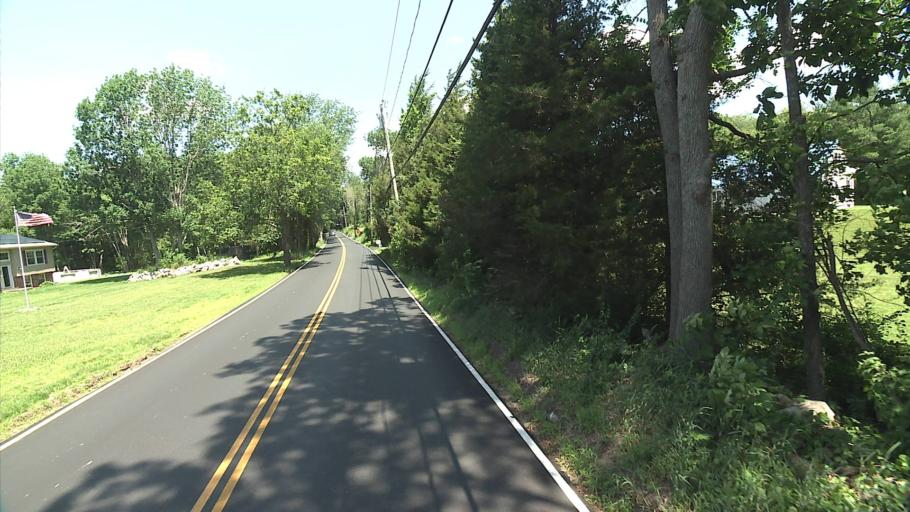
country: US
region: Connecticut
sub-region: New London County
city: Preston City
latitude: 41.5676
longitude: -71.8917
